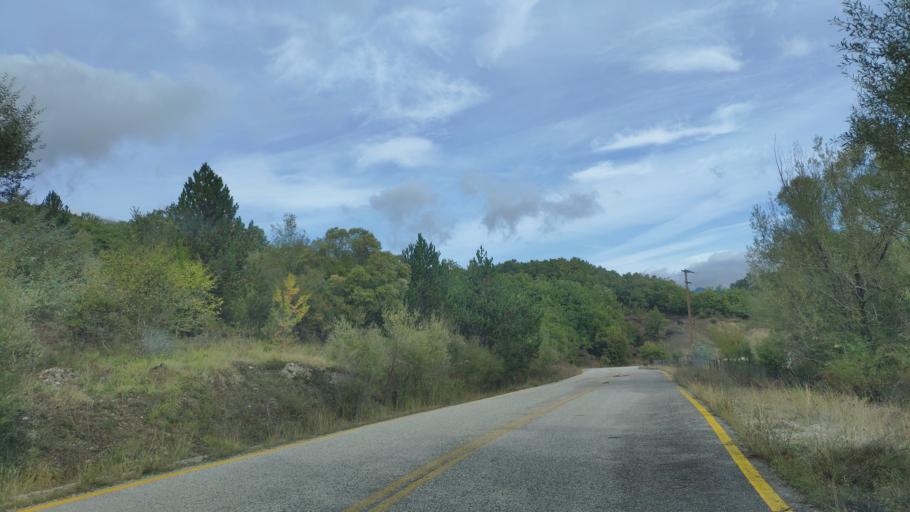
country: GR
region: West Macedonia
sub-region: Nomos Kastorias
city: Nestorio
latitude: 40.2455
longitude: 20.9881
